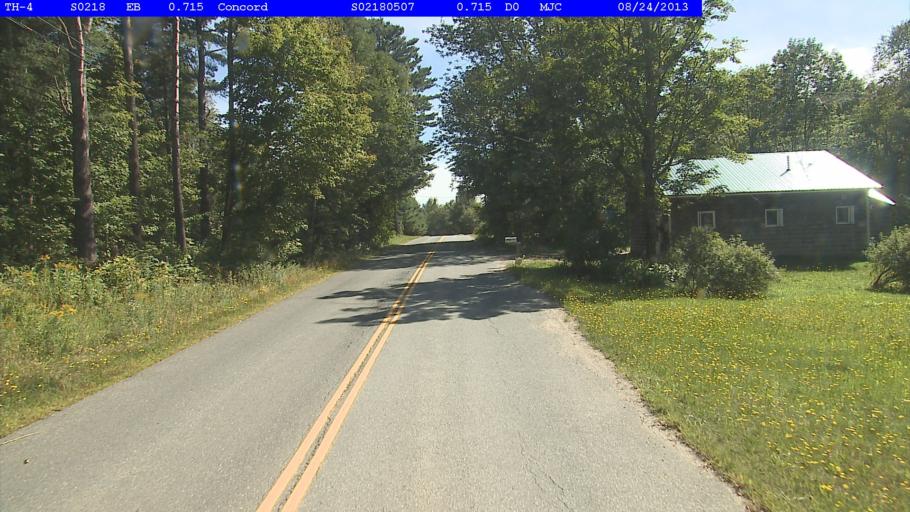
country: US
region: New Hampshire
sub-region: Grafton County
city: Littleton
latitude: 44.4553
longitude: -71.7703
